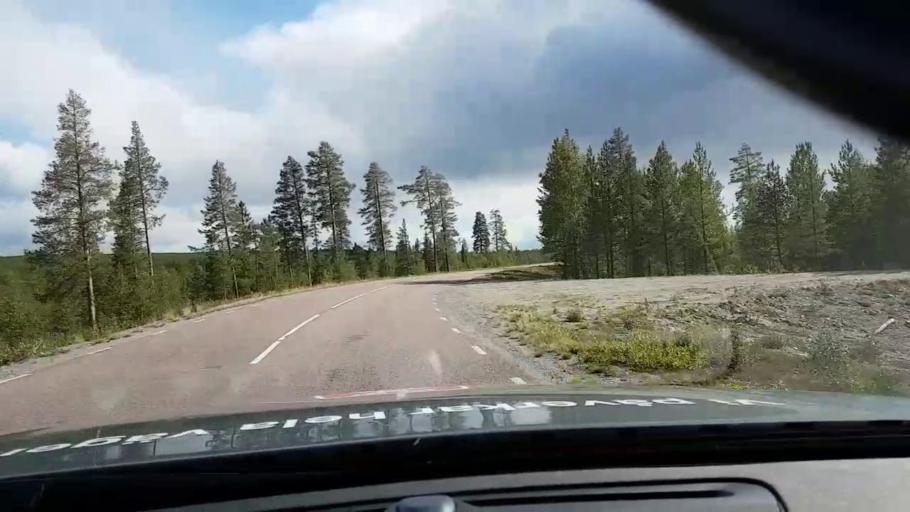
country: SE
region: Vaesterbotten
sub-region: Asele Kommun
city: Asele
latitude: 63.9023
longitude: 17.3469
